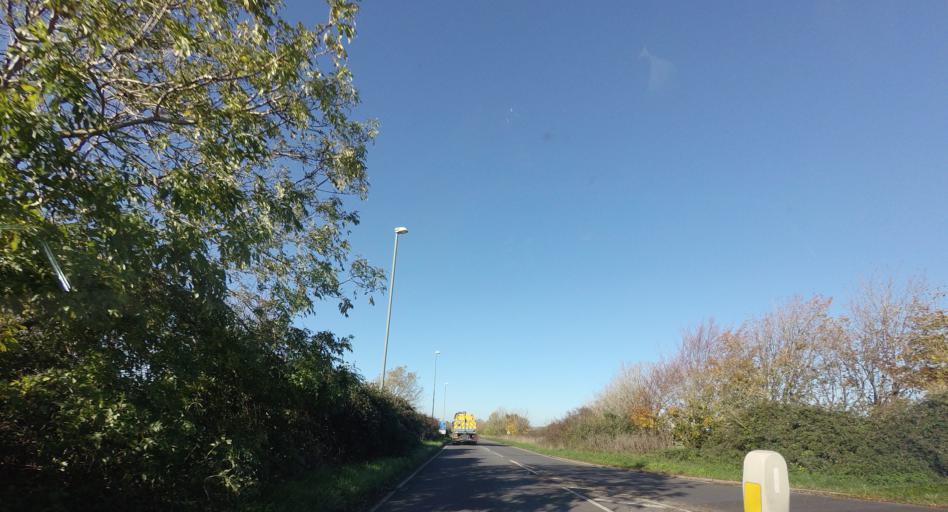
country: GB
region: England
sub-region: West Sussex
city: Steyning
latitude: 50.8751
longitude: -0.3005
